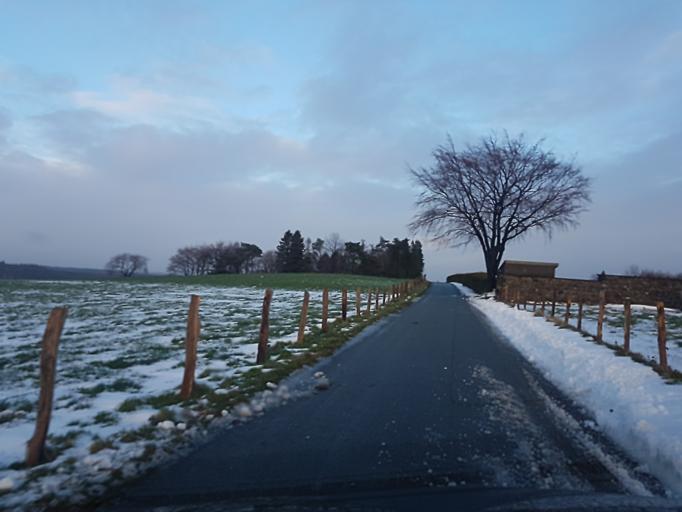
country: BE
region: Wallonia
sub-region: Province de Liege
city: Spa
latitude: 50.4748
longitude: 5.8440
